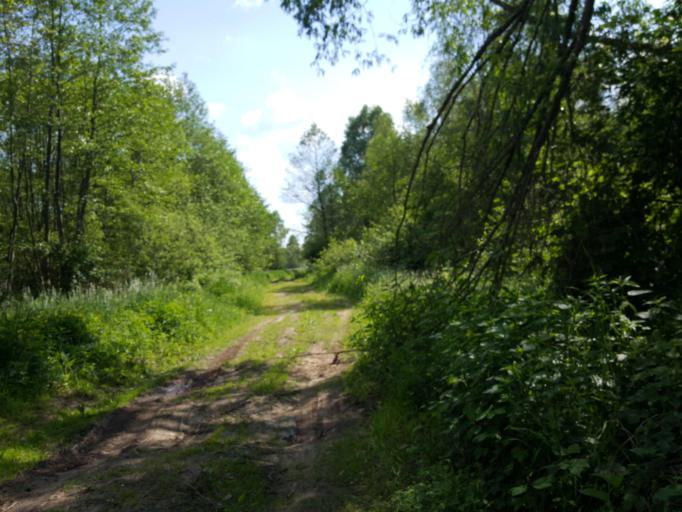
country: BY
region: Brest
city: Kamyanyets
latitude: 52.4653
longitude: 23.5913
